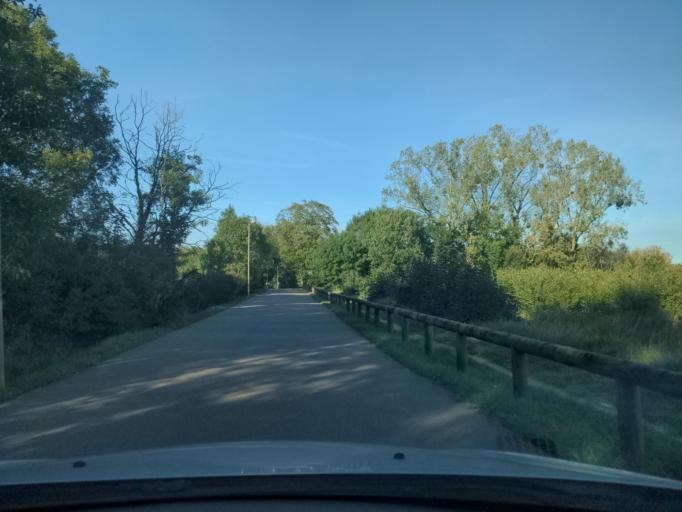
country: FR
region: Bourgogne
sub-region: Departement de la Cote-d'Or
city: Ruffey-les-Echirey
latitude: 47.3822
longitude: 5.0725
